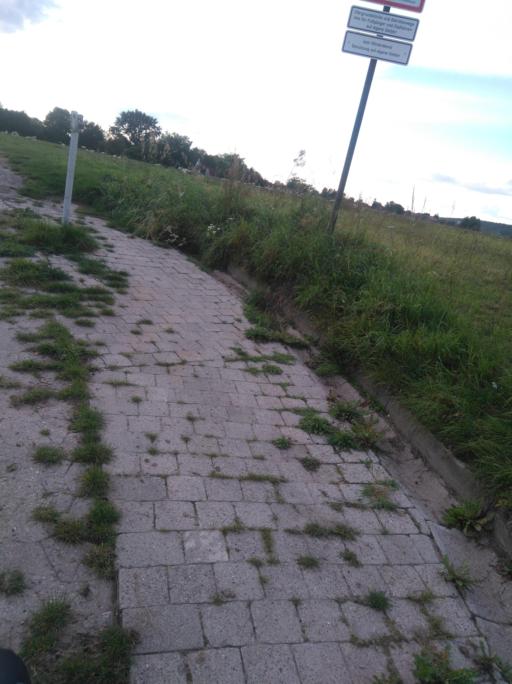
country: DE
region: Schleswig-Holstein
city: Schnakenbek
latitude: 53.3697
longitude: 10.5030
